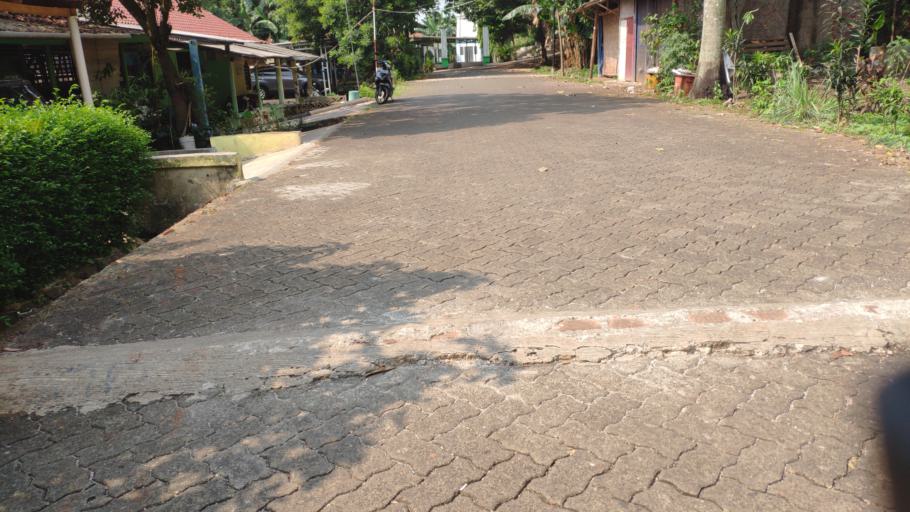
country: ID
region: West Java
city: Pamulang
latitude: -6.3153
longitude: 106.8108
